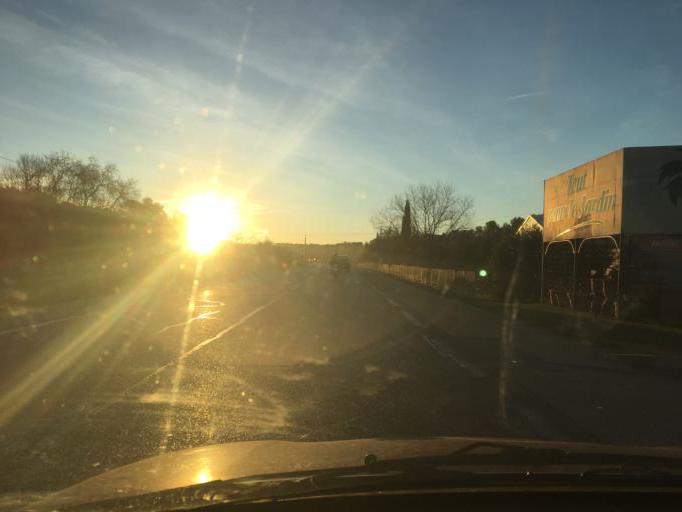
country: FR
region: Provence-Alpes-Cote d'Azur
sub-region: Departement du Var
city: Lorgues
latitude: 43.4715
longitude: 6.3803
